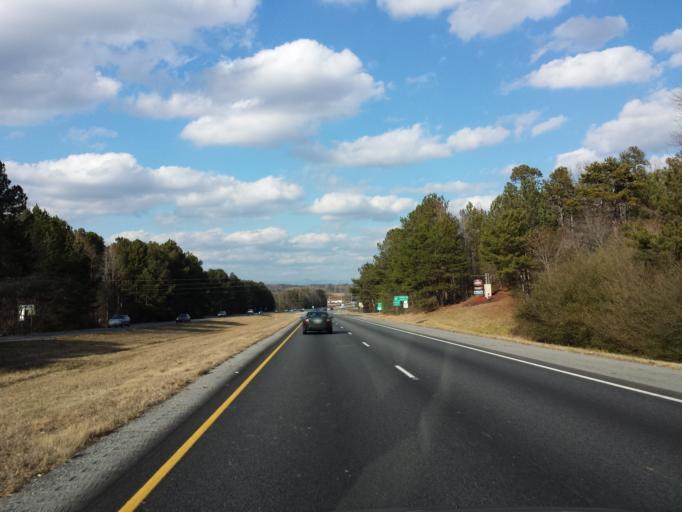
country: US
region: Georgia
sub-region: Dawson County
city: Dawsonville
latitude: 34.3339
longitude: -84.0558
